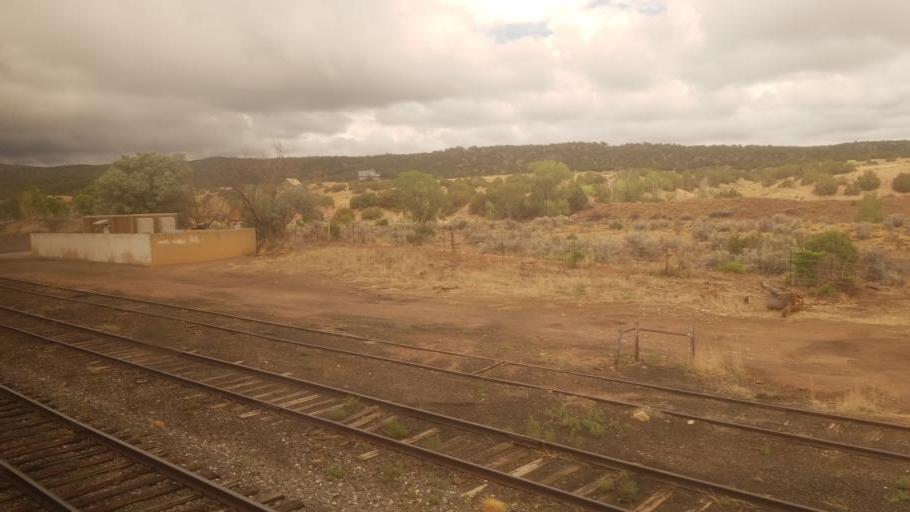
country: US
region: New Mexico
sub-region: Santa Fe County
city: Eldorado at Santa Fe
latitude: 35.4794
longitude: -105.8818
